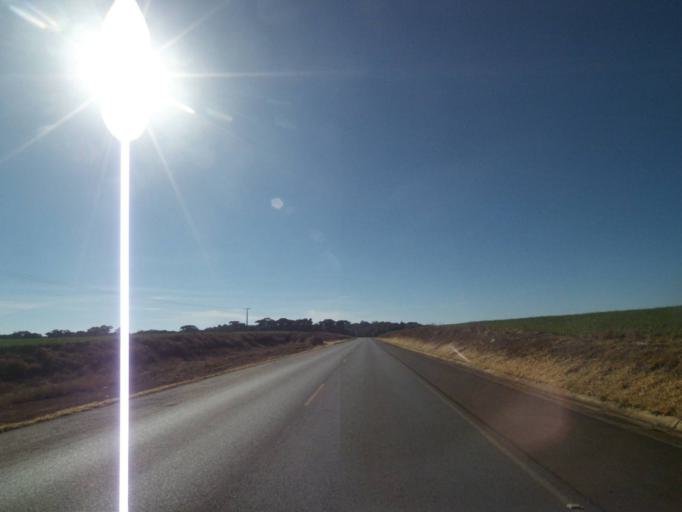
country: BR
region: Parana
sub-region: Tibagi
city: Tibagi
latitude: -24.4285
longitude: -50.4033
